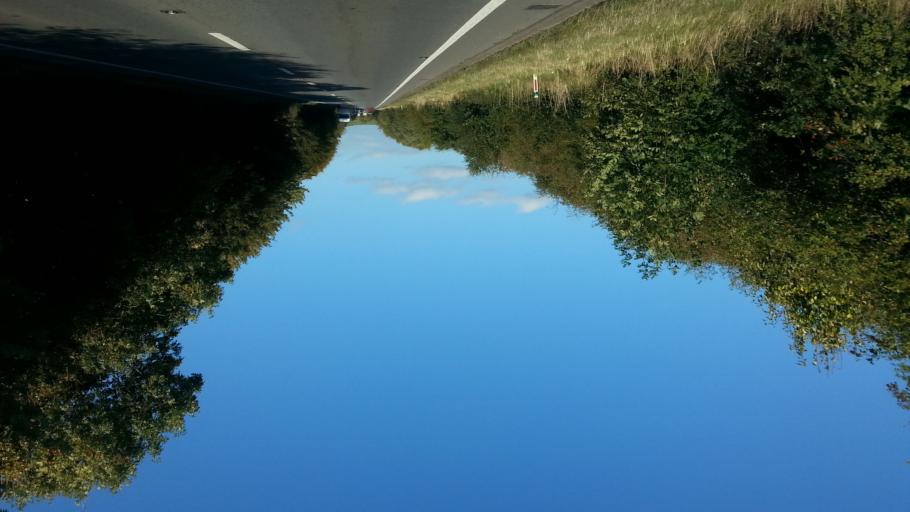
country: GB
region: England
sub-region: Northamptonshire
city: Stanwick
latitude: 52.3360
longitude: -0.5728
